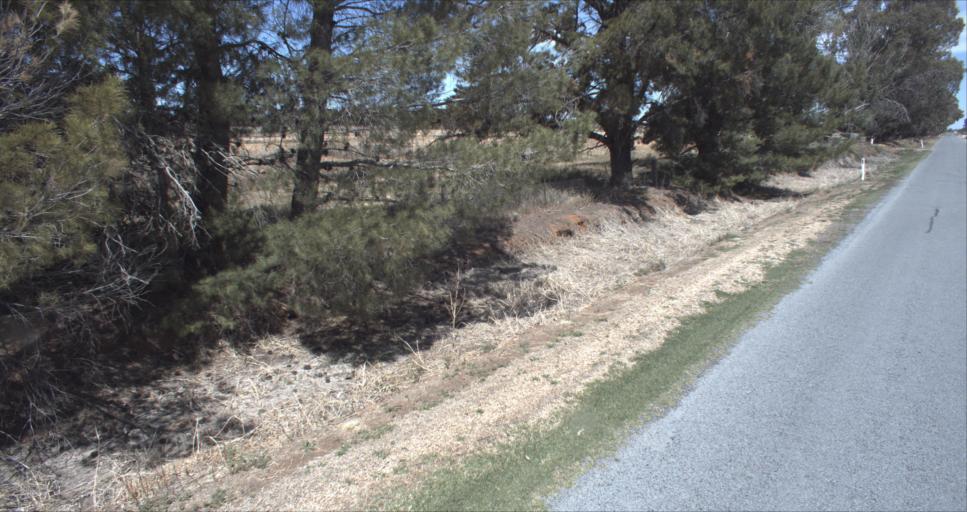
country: AU
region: New South Wales
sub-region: Leeton
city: Leeton
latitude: -34.5767
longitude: 146.4213
